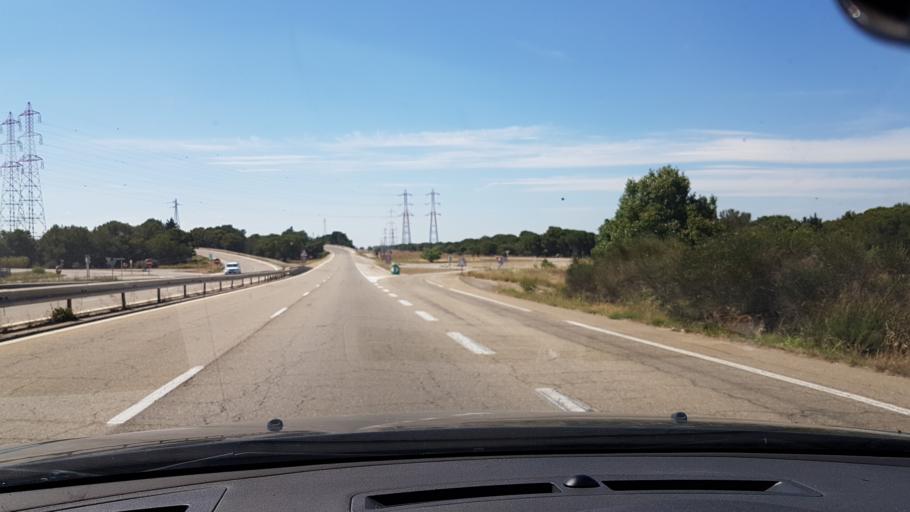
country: FR
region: Provence-Alpes-Cote d'Azur
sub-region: Departement des Bouches-du-Rhone
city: Fos-sur-Mer
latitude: 43.4762
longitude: 4.8998
